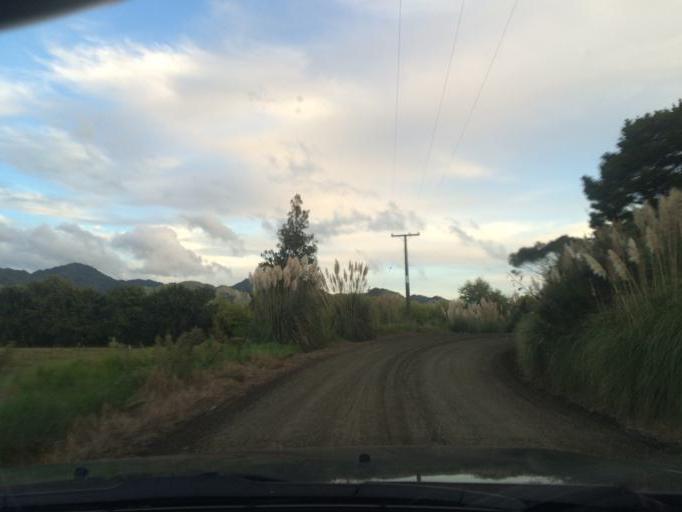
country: NZ
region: Northland
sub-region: Whangarei
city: Maungatapere
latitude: -35.8187
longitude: 174.0402
